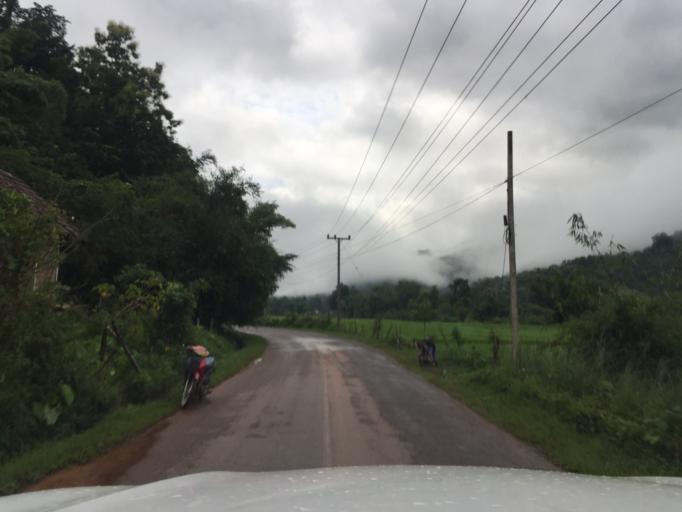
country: LA
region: Oudomxai
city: Muang La
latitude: 20.8460
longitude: 102.1055
